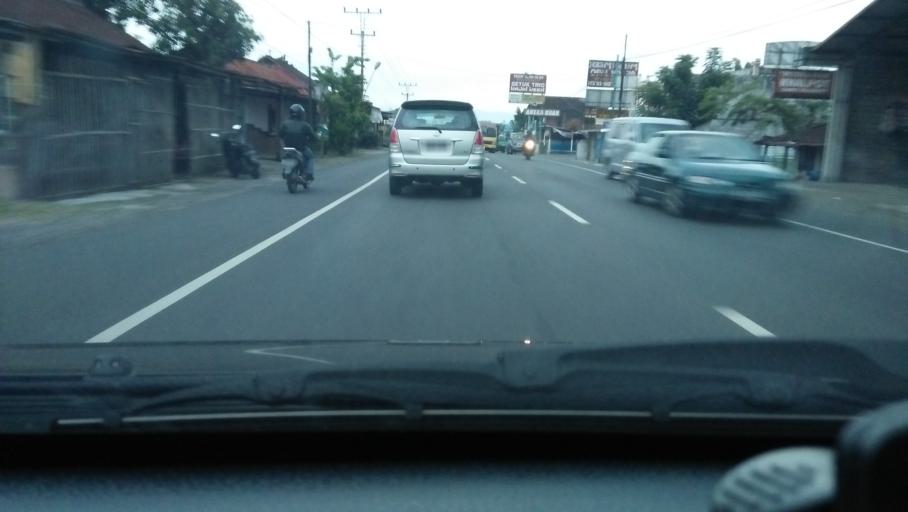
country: ID
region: Central Java
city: Magelang
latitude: -7.4204
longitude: 110.2329
